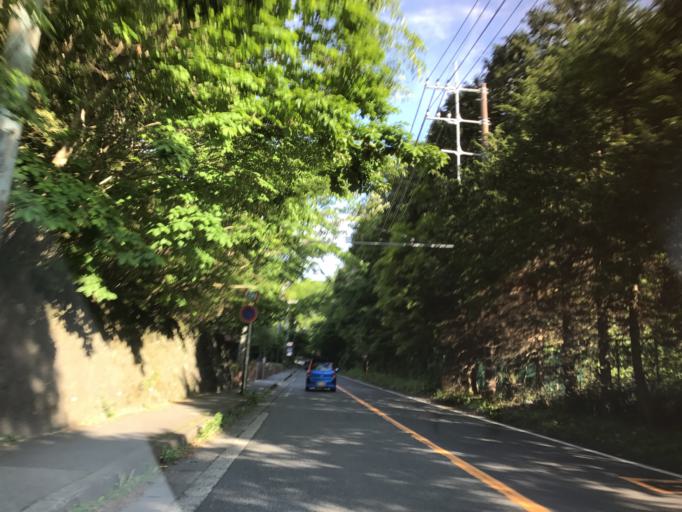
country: JP
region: Shizuoka
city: Gotemba
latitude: 35.2702
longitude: 139.0132
